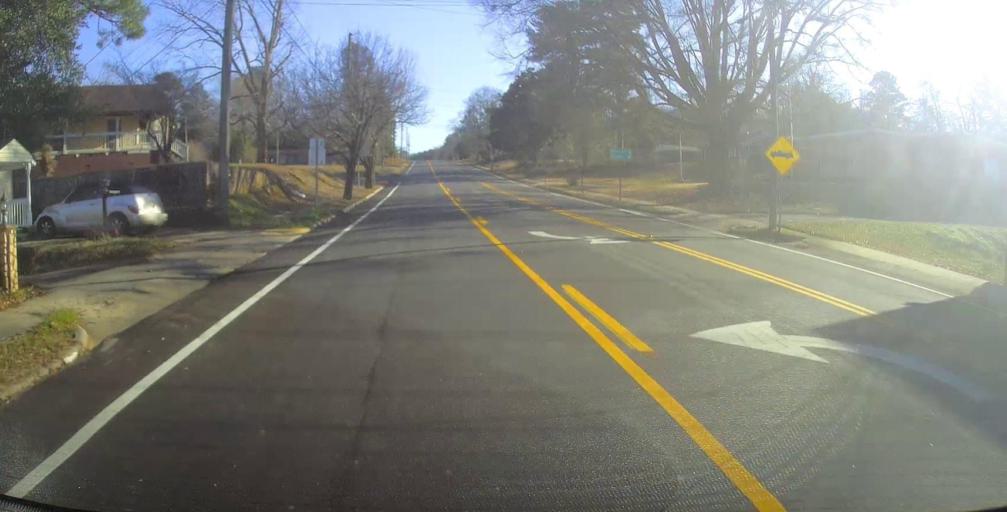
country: US
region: Georgia
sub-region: Meriwether County
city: Manchester
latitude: 32.8896
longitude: -84.6810
